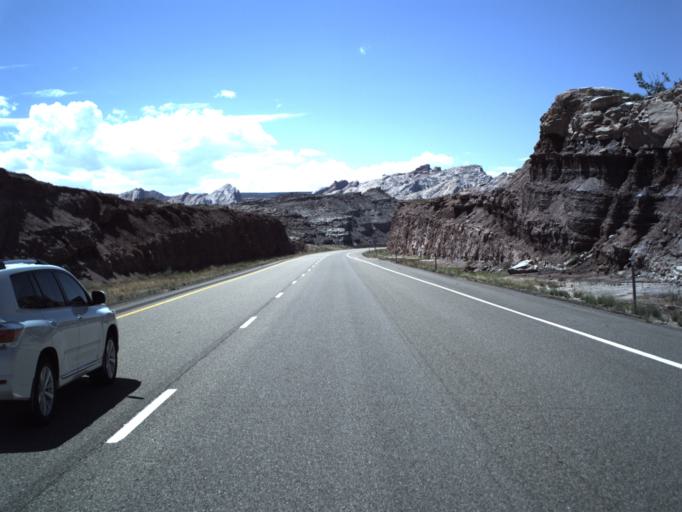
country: US
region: Utah
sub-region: Carbon County
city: East Carbon City
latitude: 38.9220
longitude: -110.3855
